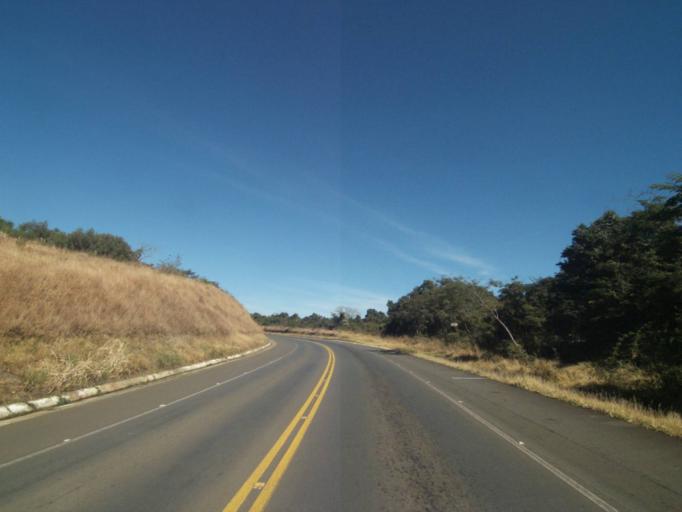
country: BR
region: Parana
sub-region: Tibagi
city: Tibagi
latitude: -24.7553
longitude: -50.4687
